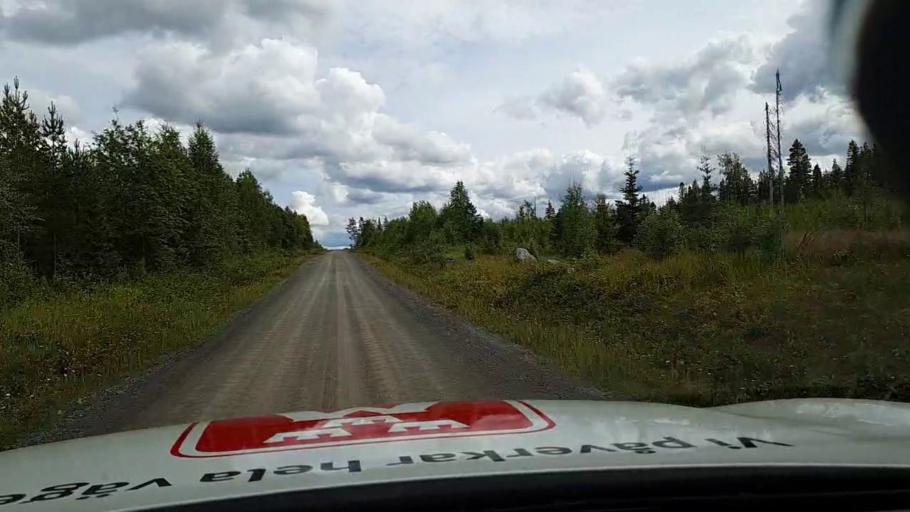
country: SE
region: Jaemtland
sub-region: OEstersunds Kommun
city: Lit
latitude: 63.2998
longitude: 15.3179
